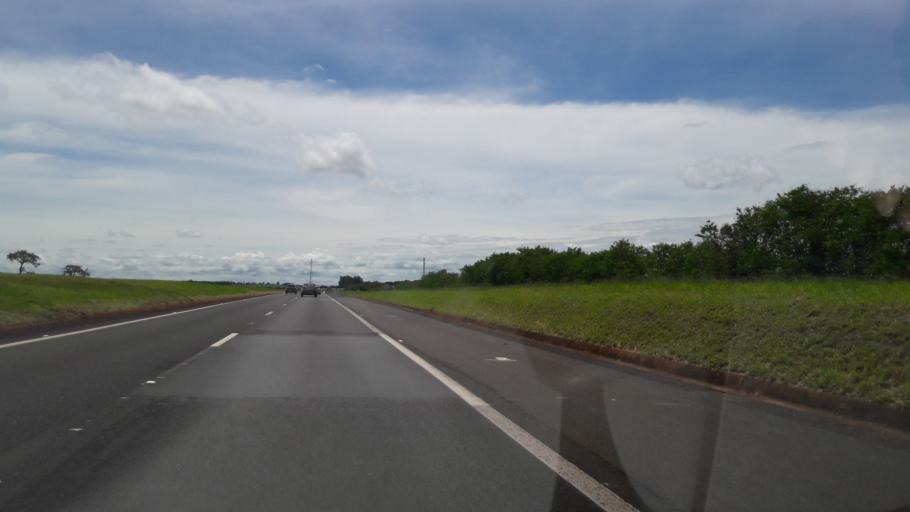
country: BR
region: Sao Paulo
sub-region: Avare
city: Avare
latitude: -22.9566
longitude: -48.8475
